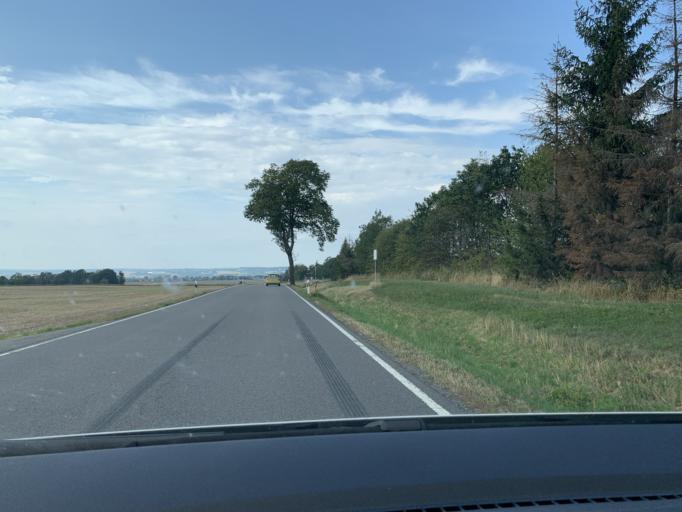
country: DE
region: Saxony
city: Frankenberg
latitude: 50.9081
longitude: 13.0896
